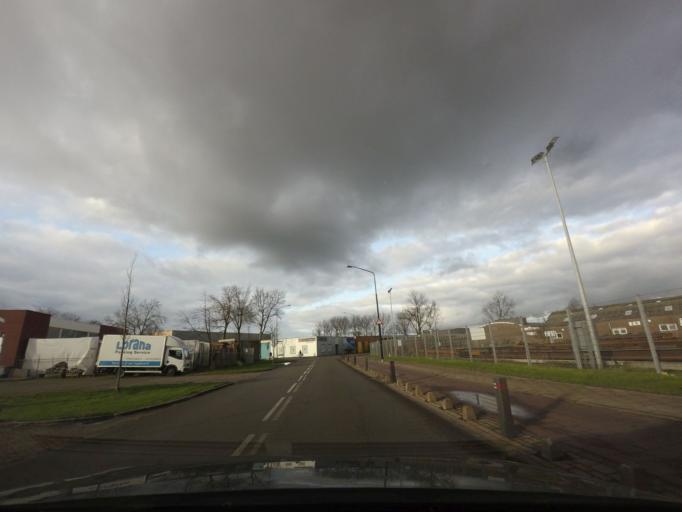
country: NL
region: North Holland
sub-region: Gemeente Heerhugowaard
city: Heerhugowaard
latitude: 52.6750
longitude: 4.8311
